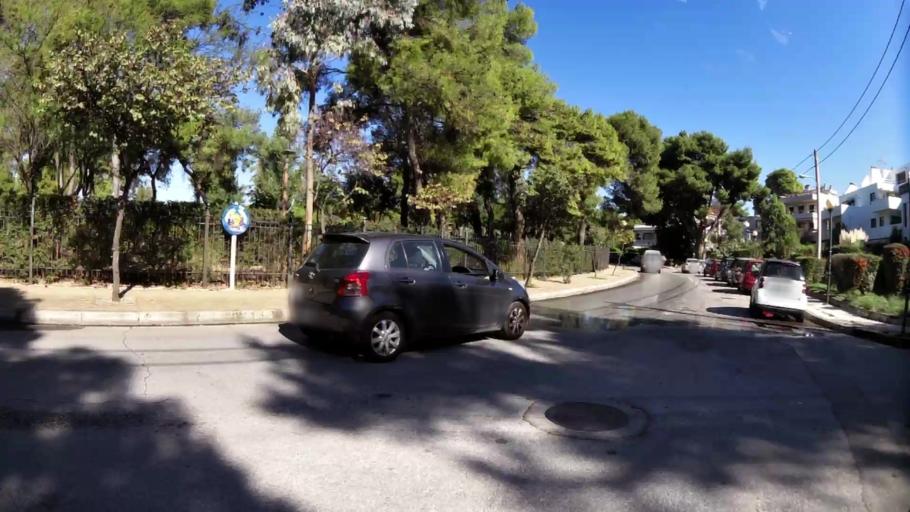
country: GR
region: Attica
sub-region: Nomarchia Athinas
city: Nea Erythraia
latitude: 38.0916
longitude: 23.8016
